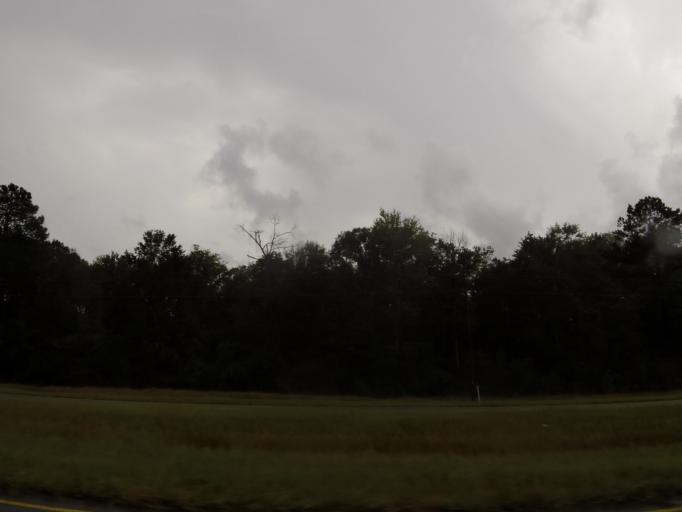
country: US
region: Georgia
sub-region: Wayne County
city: Jesup
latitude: 31.4698
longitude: -81.7198
